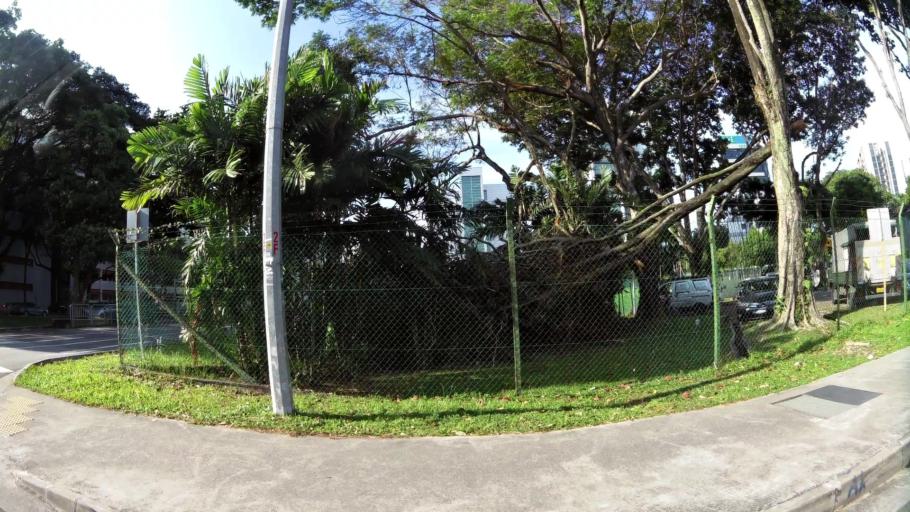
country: SG
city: Singapore
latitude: 1.3283
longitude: 103.8718
